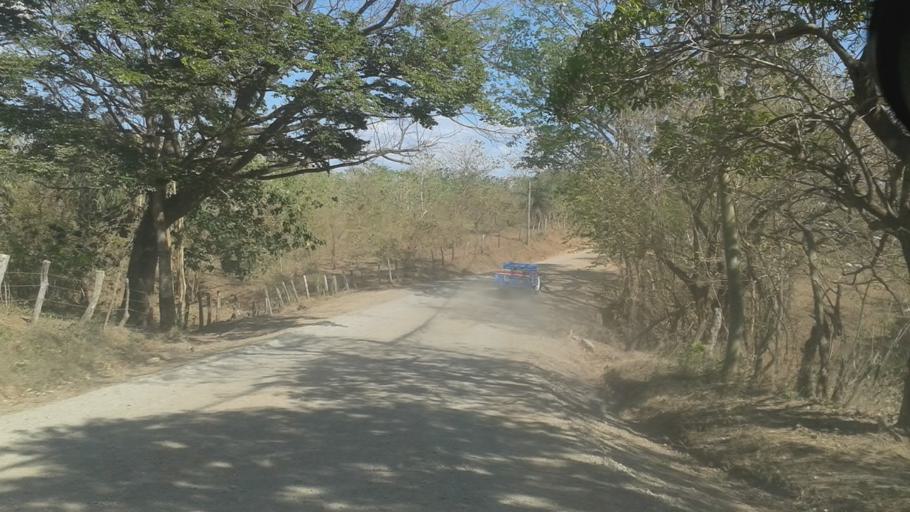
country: CR
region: Guanacaste
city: Santa Cruz
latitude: 10.1036
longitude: -85.7641
